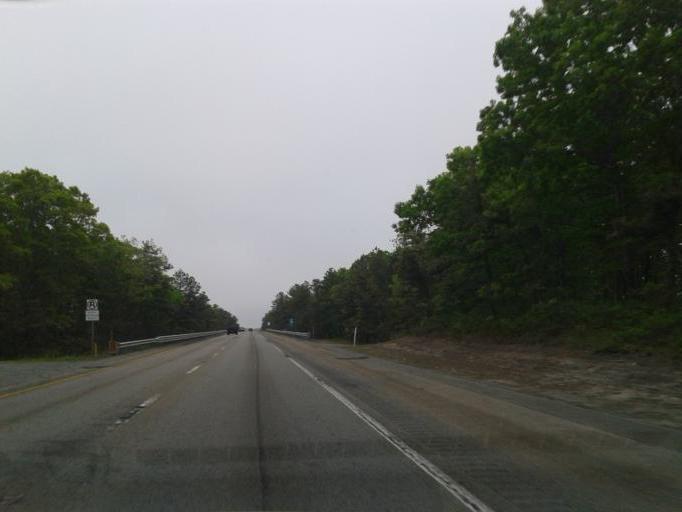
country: US
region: Massachusetts
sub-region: Plymouth County
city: Plymouth
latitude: 41.8966
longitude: -70.6148
